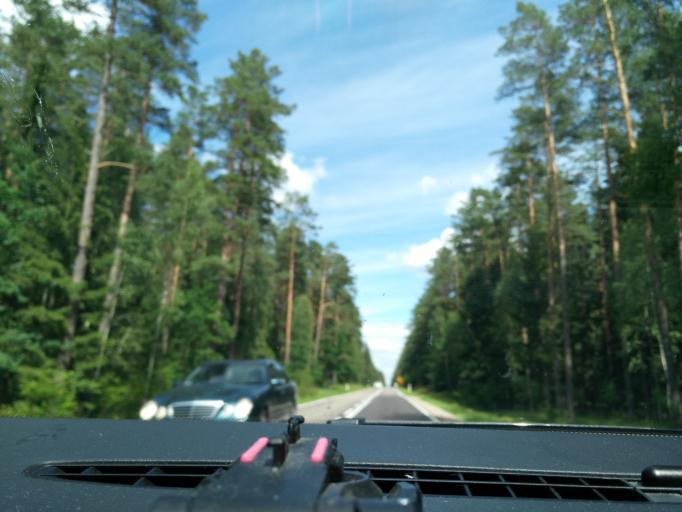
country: PL
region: Podlasie
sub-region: Powiat sejnenski
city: Krasnopol
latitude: 53.9620
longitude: 23.2319
